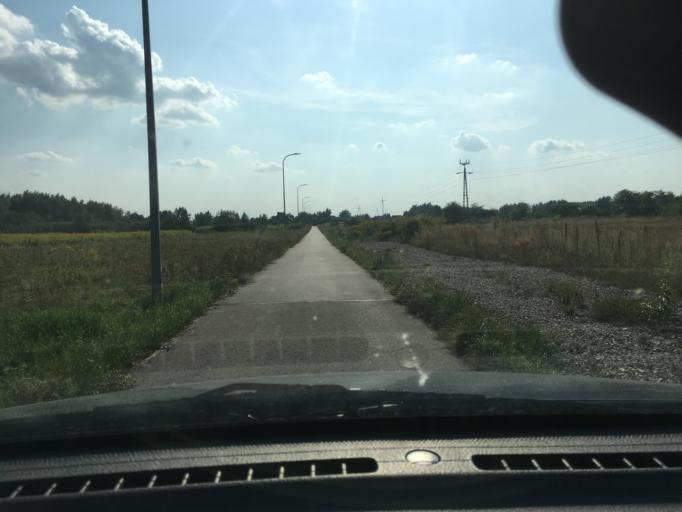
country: PL
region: Masovian Voivodeship
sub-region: Powiat piaseczynski
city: Lesznowola
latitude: 52.0542
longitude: 20.9381
